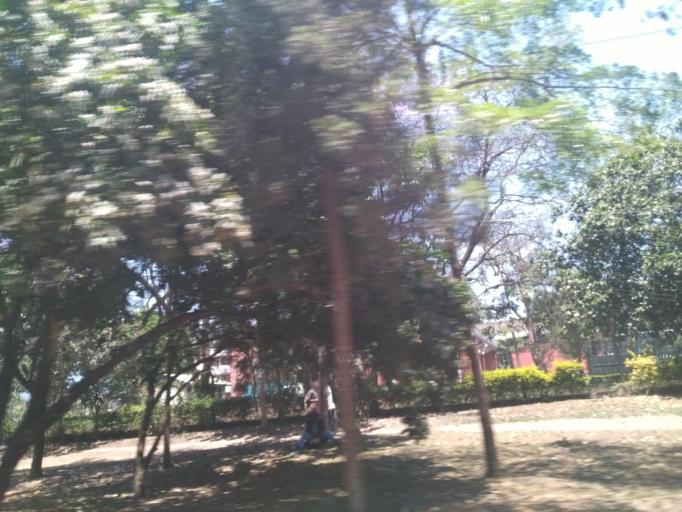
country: TZ
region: Arusha
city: Arusha
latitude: -3.3640
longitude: 36.6765
